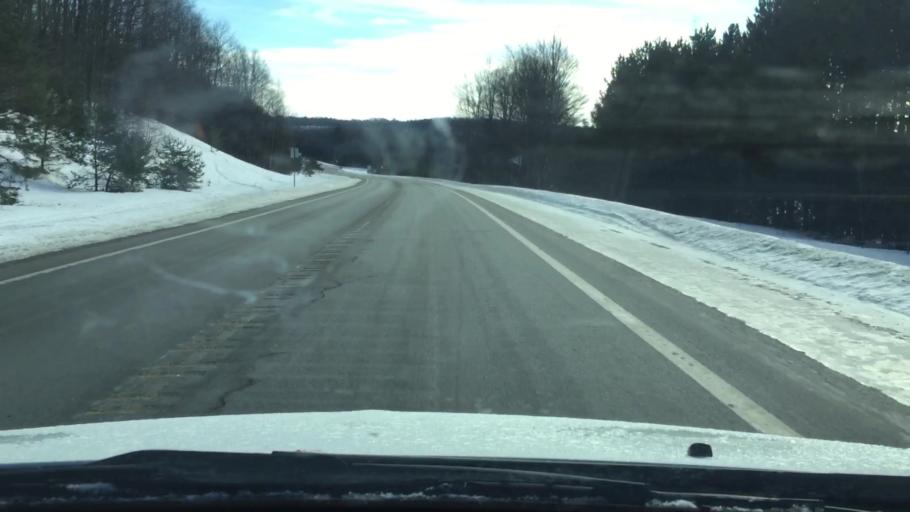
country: US
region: Michigan
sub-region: Antrim County
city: Mancelona
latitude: 44.9713
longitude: -85.0549
